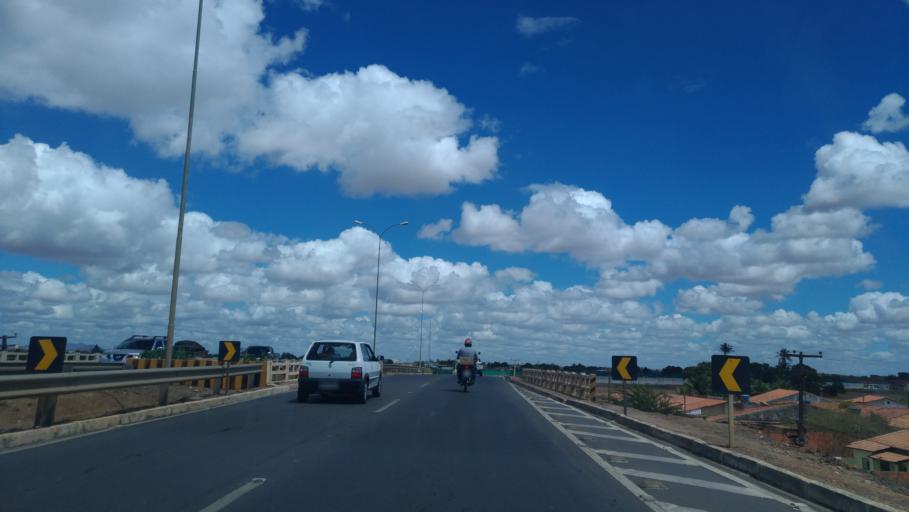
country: BR
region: Alagoas
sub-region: Arapiraca
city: Arapiraca
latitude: -9.7314
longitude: -36.6580
